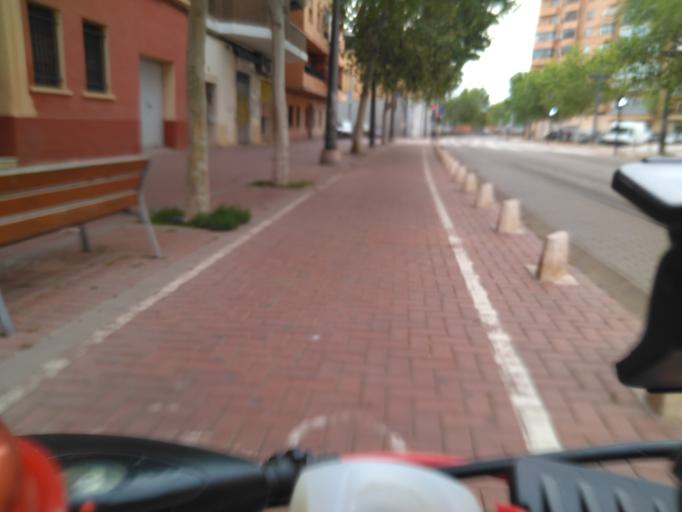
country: ES
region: Valencia
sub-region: Provincia de Valencia
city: Valencia
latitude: 39.4892
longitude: -0.3853
